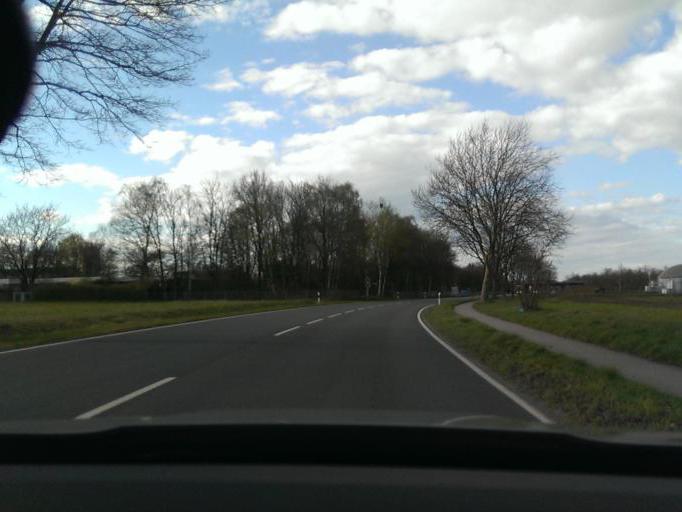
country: DE
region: Lower Saxony
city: Langenhagen
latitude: 52.4866
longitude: 9.7302
